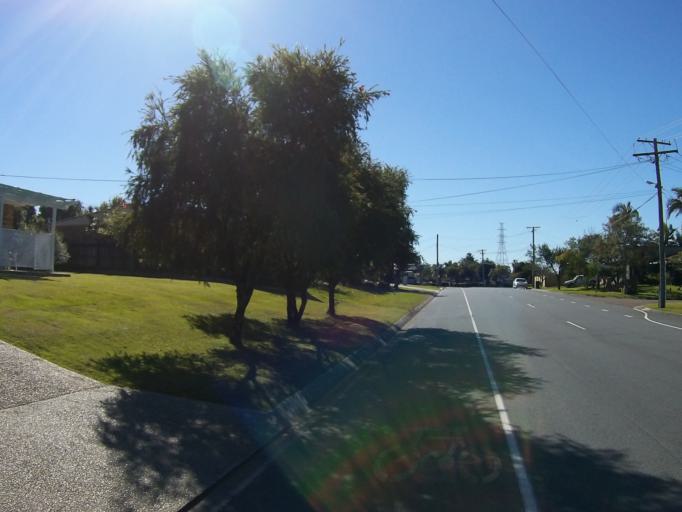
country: AU
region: Queensland
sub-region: Logan
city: Windaroo
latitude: -27.7295
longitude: 153.2128
